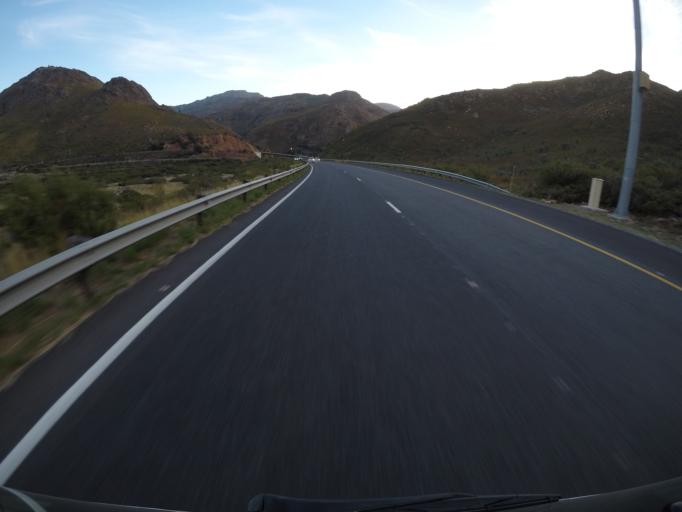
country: ZA
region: Western Cape
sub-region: Cape Winelands District Municipality
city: Paarl
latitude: -33.7278
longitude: 19.1205
